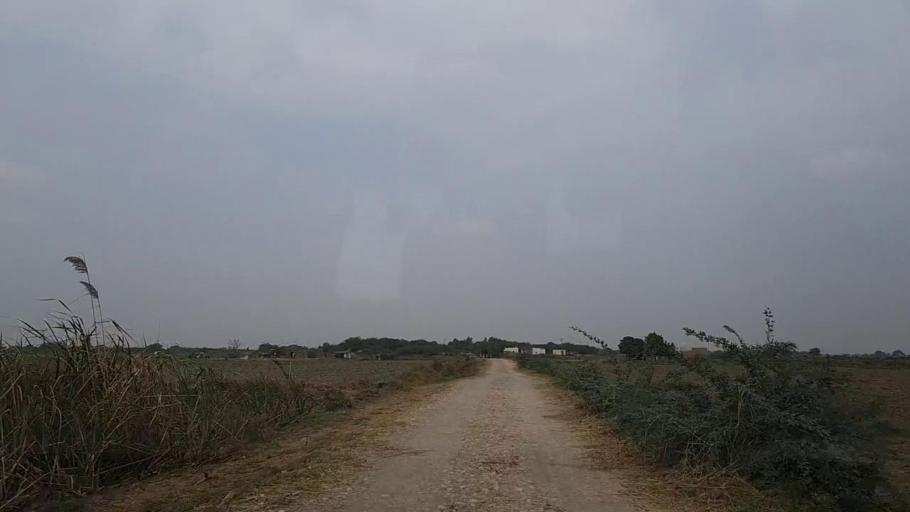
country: PK
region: Sindh
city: Mirpur Sakro
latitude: 24.6000
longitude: 67.6980
